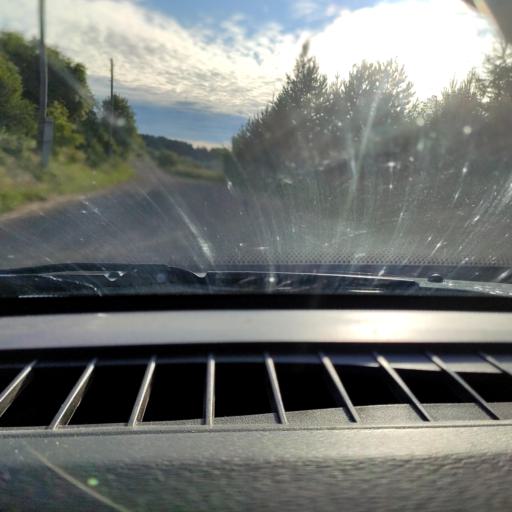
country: RU
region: Perm
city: Uinskoye
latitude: 57.1183
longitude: 56.5173
